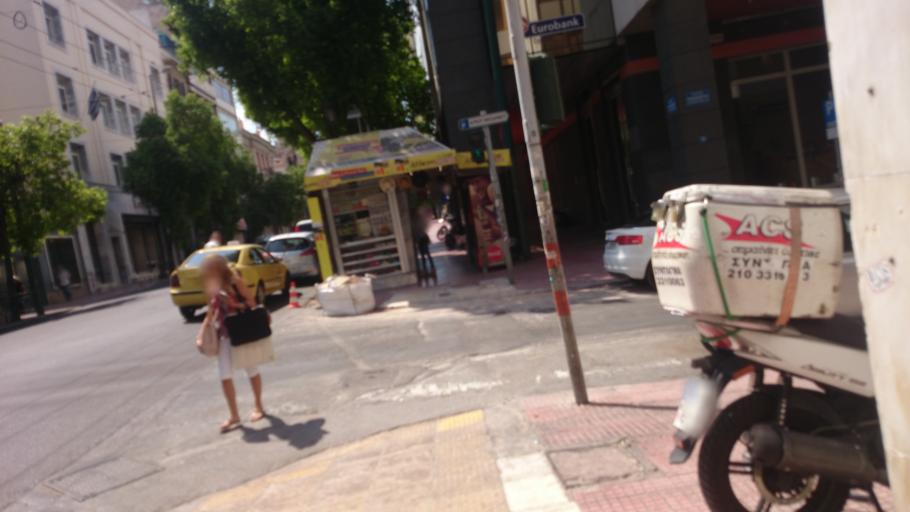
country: GR
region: Attica
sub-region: Nomarchia Athinas
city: Athens
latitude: 37.9746
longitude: 23.7340
